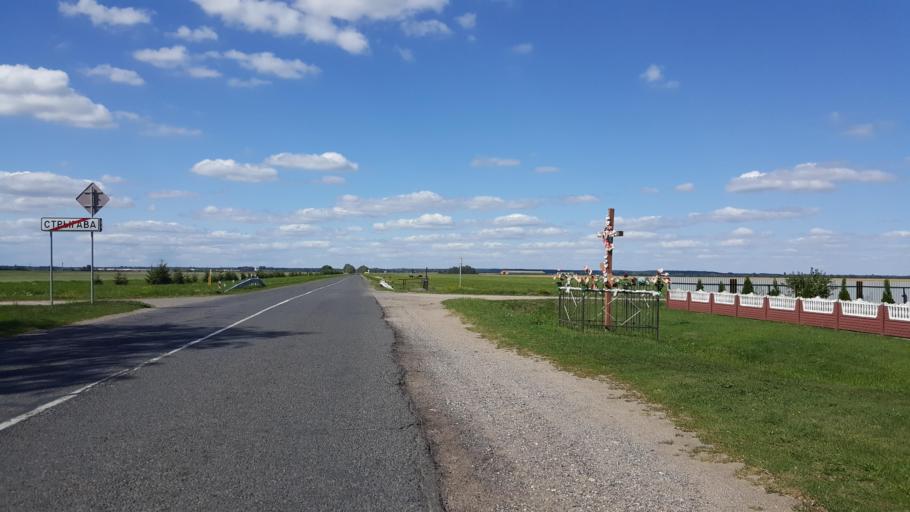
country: BY
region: Brest
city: Kobryn
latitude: 52.3089
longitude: 24.2724
